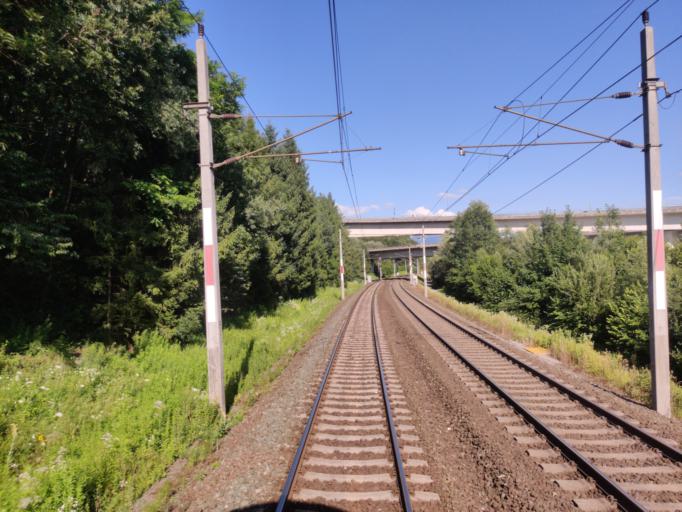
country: AT
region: Vorarlberg
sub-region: Politischer Bezirk Feldkirch
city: Feldkirch
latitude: 47.2283
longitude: 9.6154
